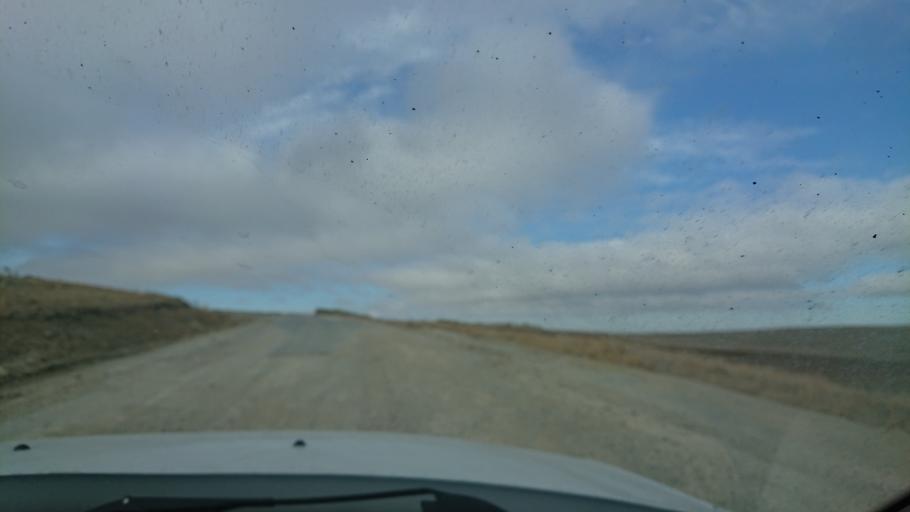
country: TR
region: Aksaray
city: Ortakoy
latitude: 38.7793
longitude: 34.0078
